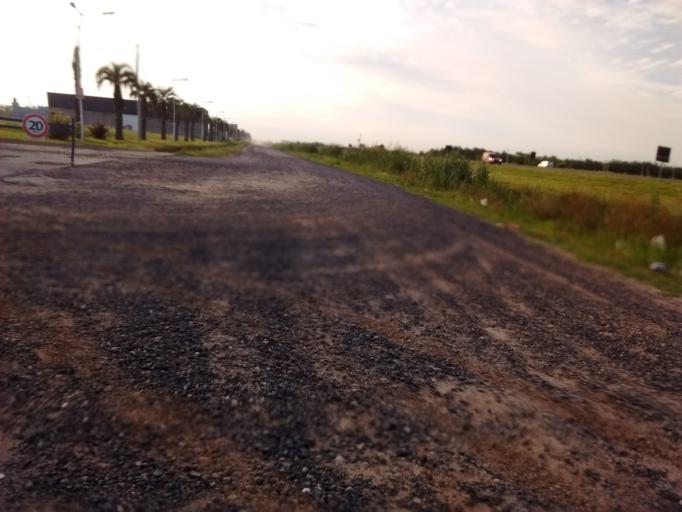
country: AR
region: Santa Fe
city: Roldan
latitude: -32.9305
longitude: -60.8752
